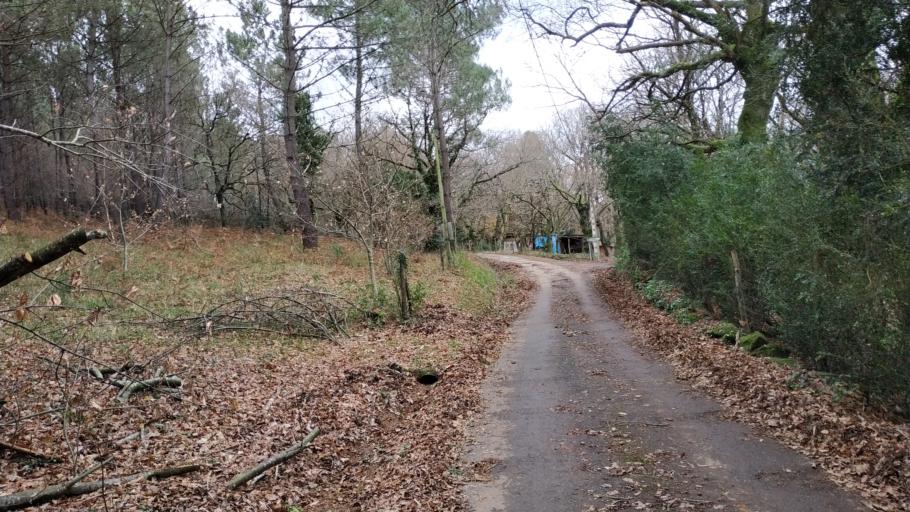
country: ES
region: Galicia
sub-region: Provincia de Pontevedra
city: Silleda
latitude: 42.7742
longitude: -8.1698
